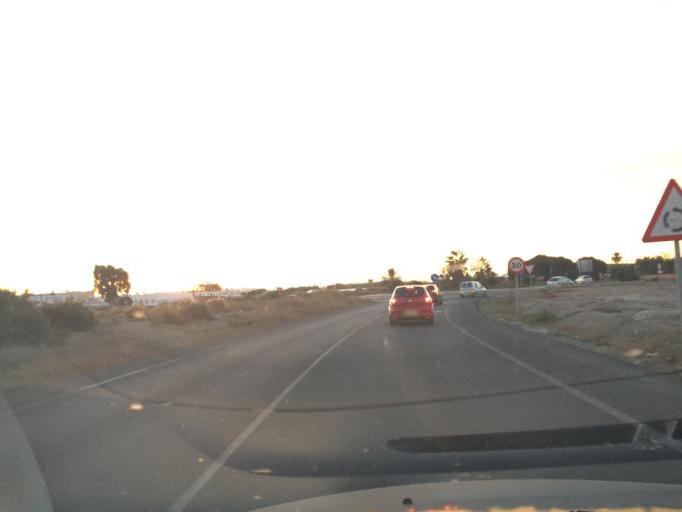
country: ES
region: Andalusia
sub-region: Provincia de Almeria
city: Almeria
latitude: 36.8405
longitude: -2.4186
